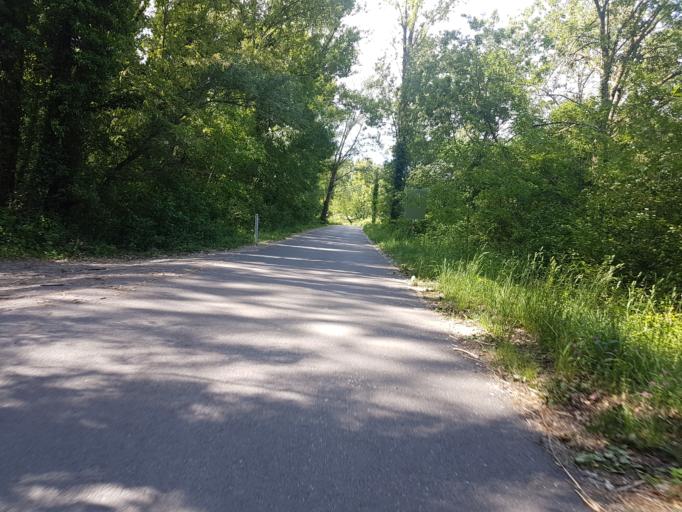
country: FR
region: Rhone-Alpes
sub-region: Departement de l'Ardeche
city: La Voulte-sur-Rhone
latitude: 44.7830
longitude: 4.7744
